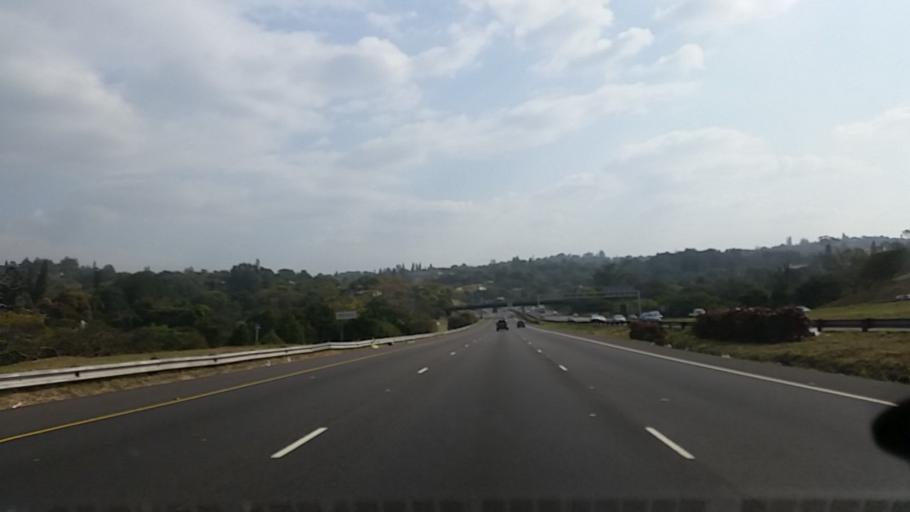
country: ZA
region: KwaZulu-Natal
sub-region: eThekwini Metropolitan Municipality
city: Berea
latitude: -29.8408
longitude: 30.9556
